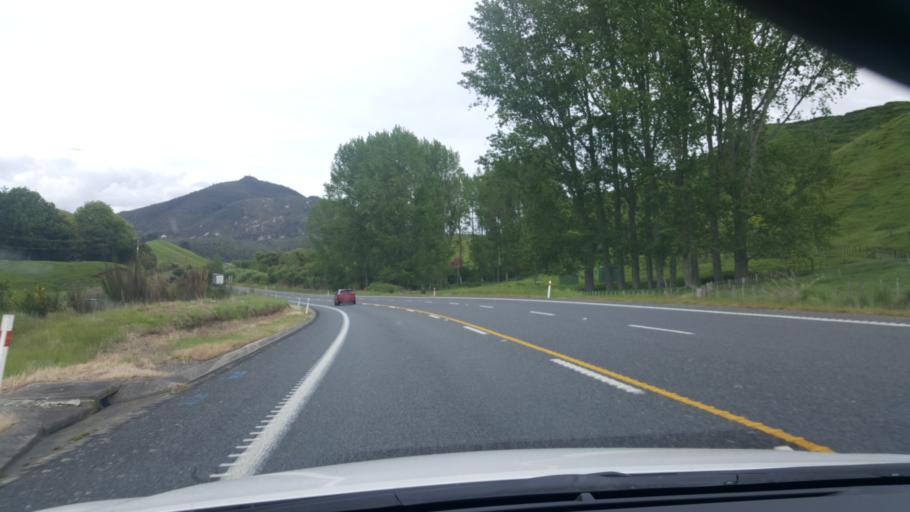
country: NZ
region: Bay of Plenty
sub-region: Rotorua District
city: Rotorua
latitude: -38.3016
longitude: 176.3653
